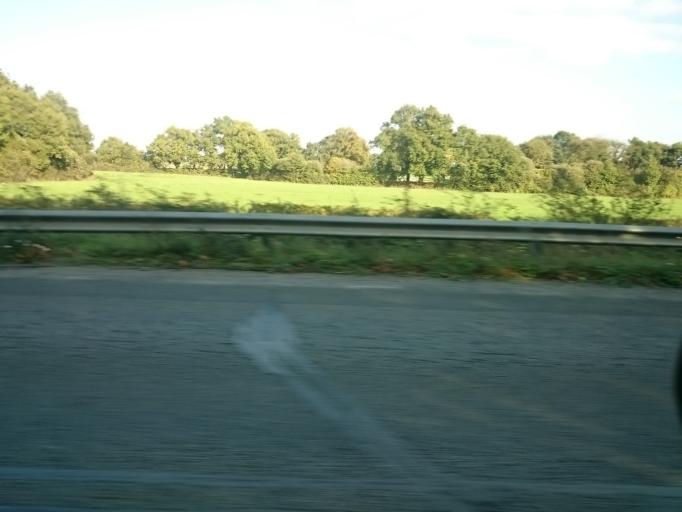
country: FR
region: Pays de la Loire
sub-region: Departement de la Loire-Atlantique
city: Heric
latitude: 47.3844
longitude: -1.6433
